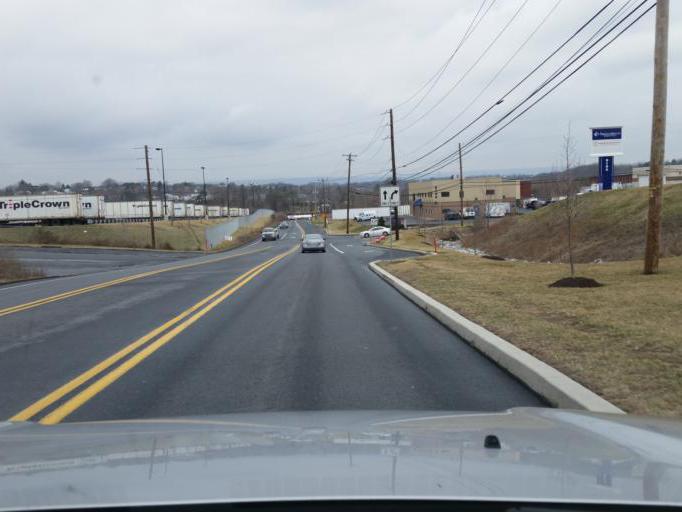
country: US
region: Pennsylvania
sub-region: Dauphin County
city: Rutherford
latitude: 40.2636
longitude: -76.7467
